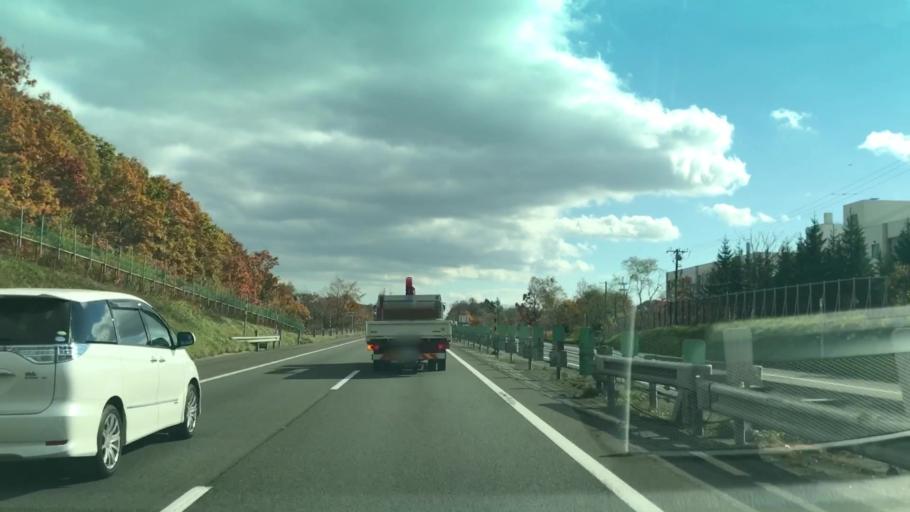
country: JP
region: Hokkaido
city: Kitahiroshima
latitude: 42.9716
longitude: 141.4857
